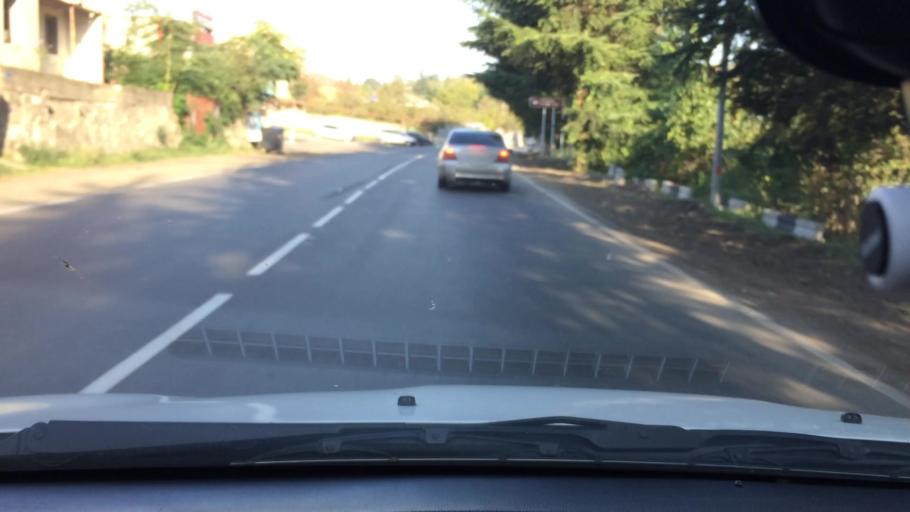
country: GE
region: Imereti
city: Zestap'oni
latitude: 42.1056
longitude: 43.0531
